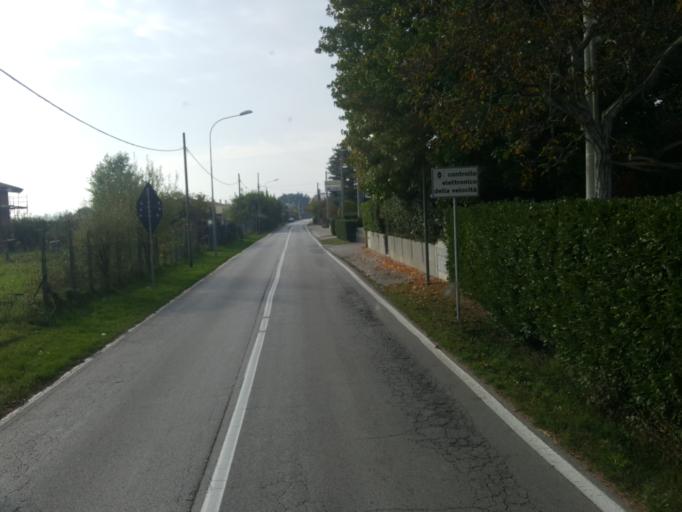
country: IT
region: Veneto
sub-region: Provincia di Vicenza
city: Rossano Veneto
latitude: 45.7178
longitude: 11.8206
